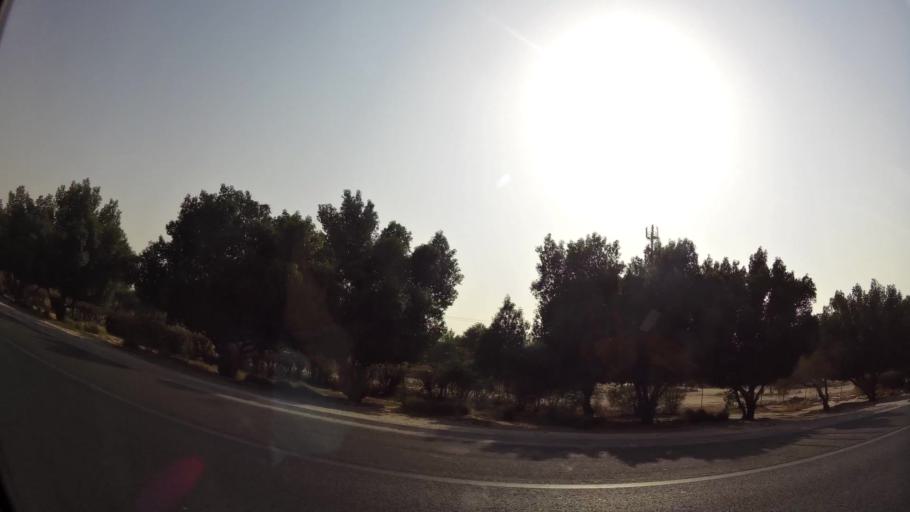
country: KW
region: Muhafazat al Jahra'
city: Al Jahra'
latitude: 29.3325
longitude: 47.7311
